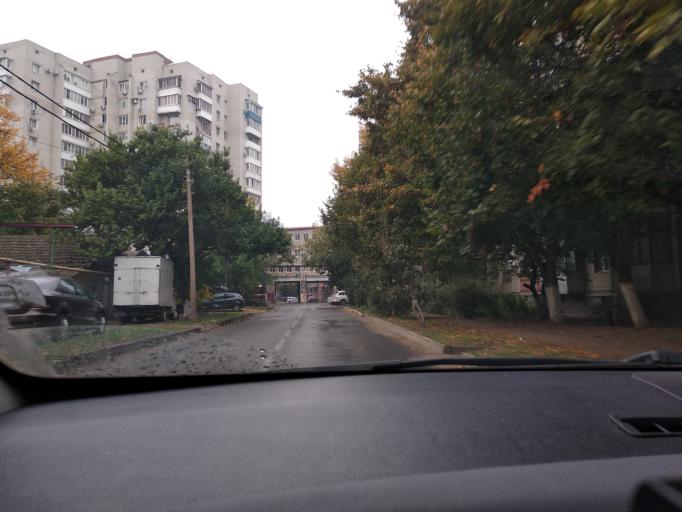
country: RU
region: Krasnodarskiy
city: Krasnodar
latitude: 45.0175
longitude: 38.9954
